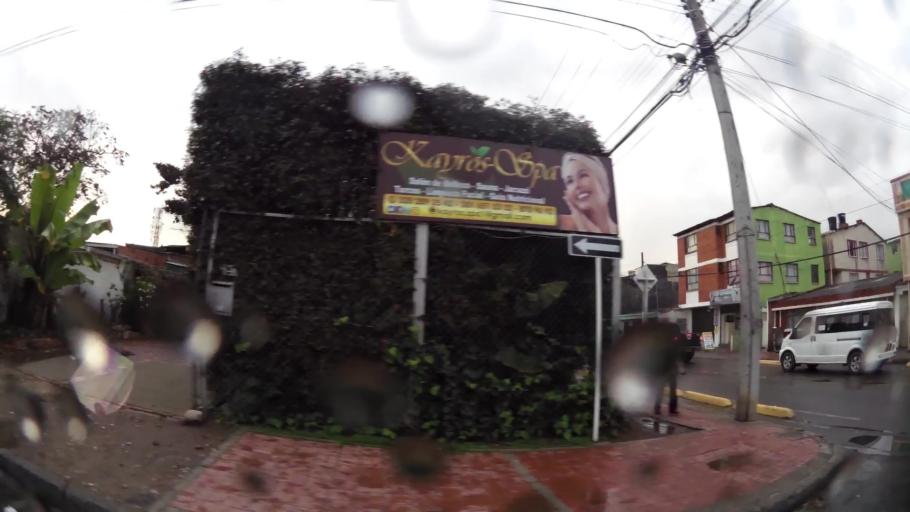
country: CO
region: Cundinamarca
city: Chia
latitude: 4.8677
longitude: -74.0537
